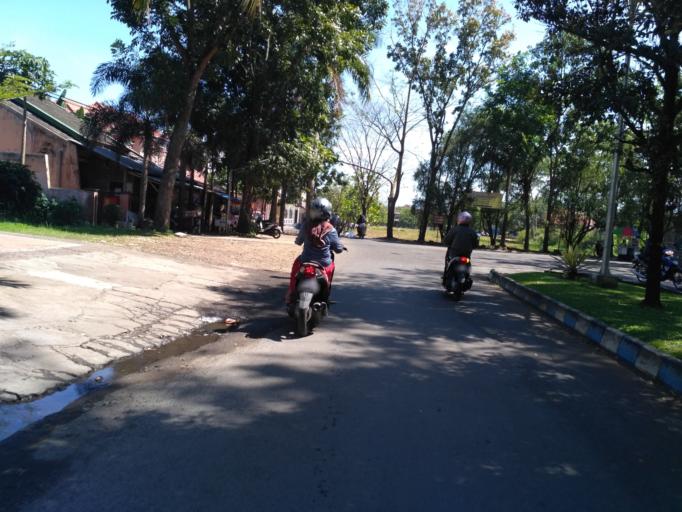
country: ID
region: East Java
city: Malang
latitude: -7.9739
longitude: 112.6690
